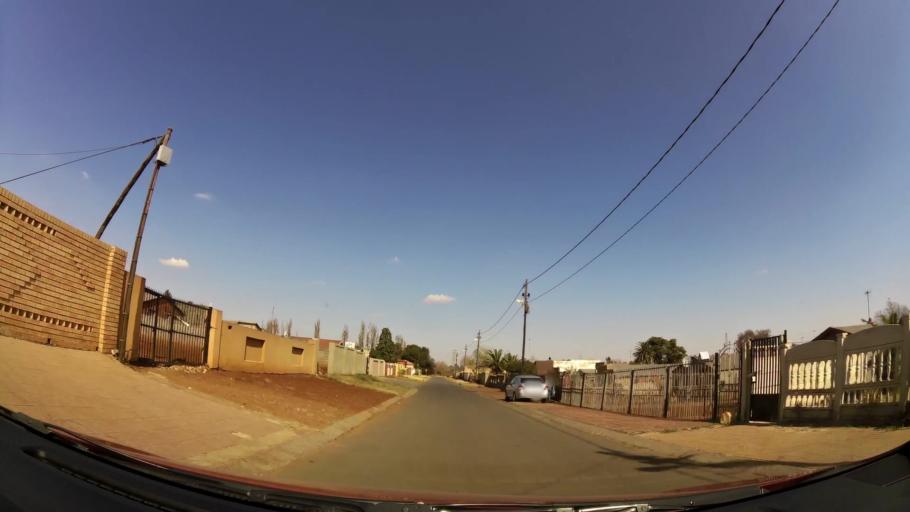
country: ZA
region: Gauteng
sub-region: City of Johannesburg Metropolitan Municipality
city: Soweto
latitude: -26.2444
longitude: 27.8918
